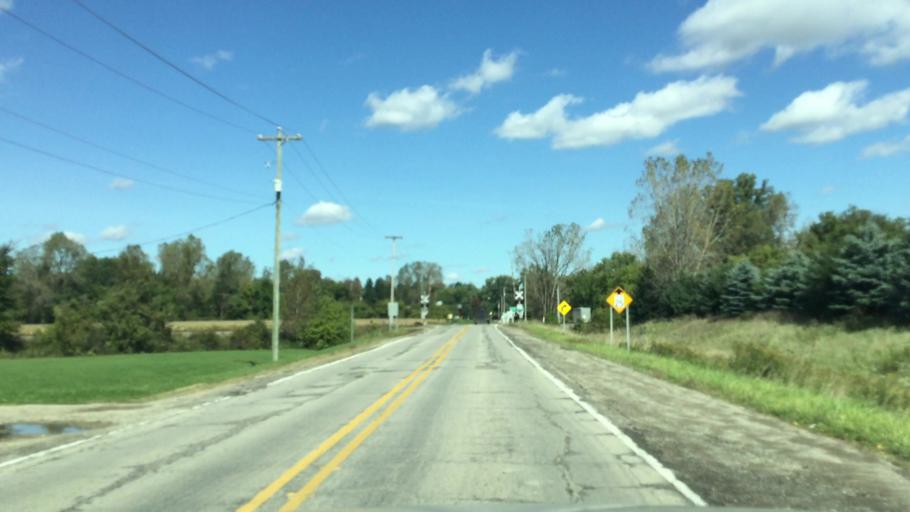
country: US
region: Michigan
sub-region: Genesee County
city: Swartz Creek
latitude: 42.9422
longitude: -83.8586
